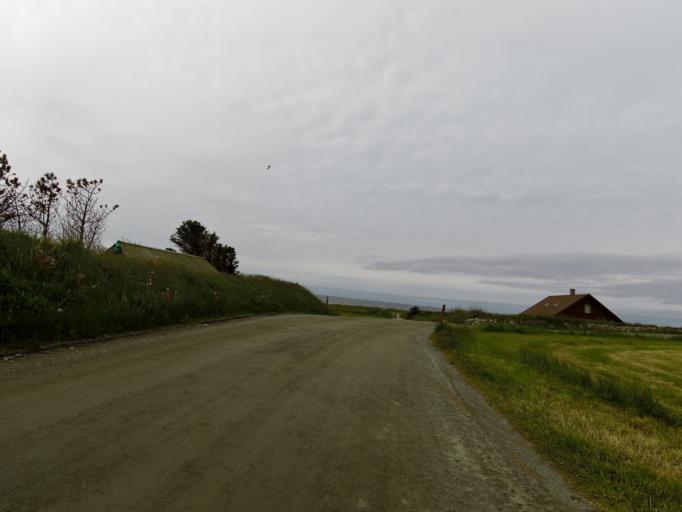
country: NO
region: Rogaland
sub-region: Klepp
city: Kleppe
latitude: 58.8136
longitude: 5.5512
